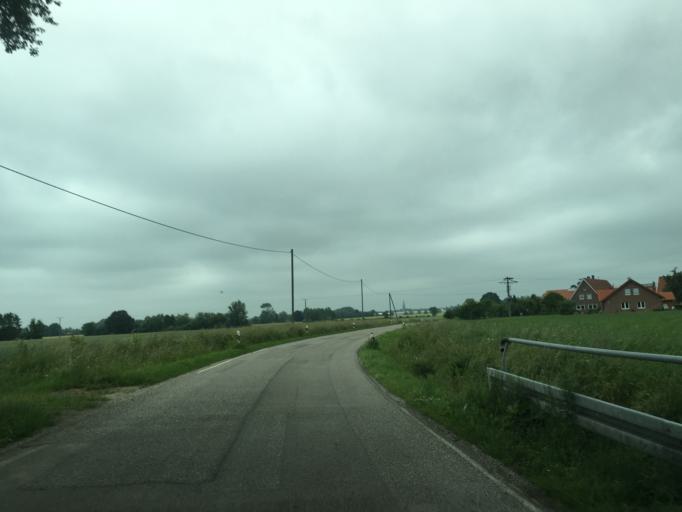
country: DE
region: North Rhine-Westphalia
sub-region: Regierungsbezirk Munster
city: Altenberge
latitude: 52.0235
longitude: 7.4601
